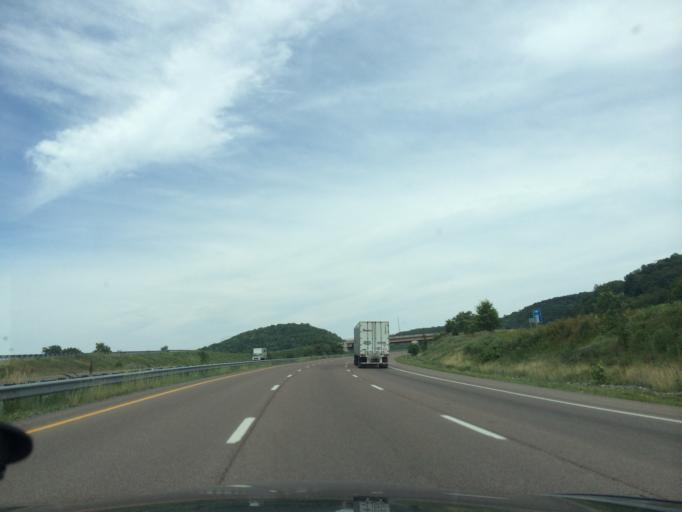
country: US
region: Maryland
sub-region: Allegany County
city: Cumberland
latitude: 39.6929
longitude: -78.6537
